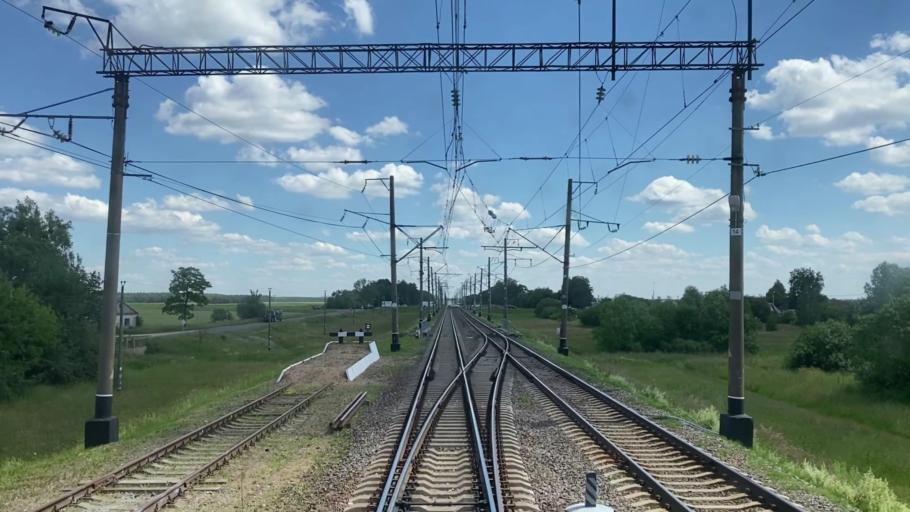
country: BY
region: Brest
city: Ivatsevichy
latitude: 52.8327
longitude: 25.4914
